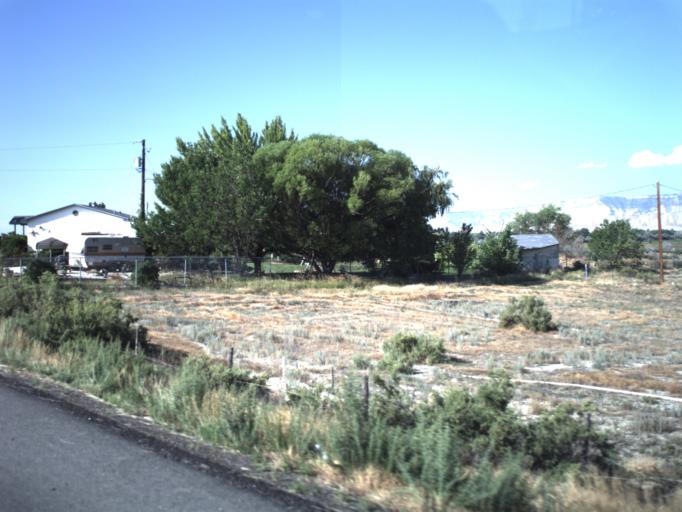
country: US
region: Utah
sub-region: Emery County
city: Huntington
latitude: 39.3185
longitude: -110.9645
